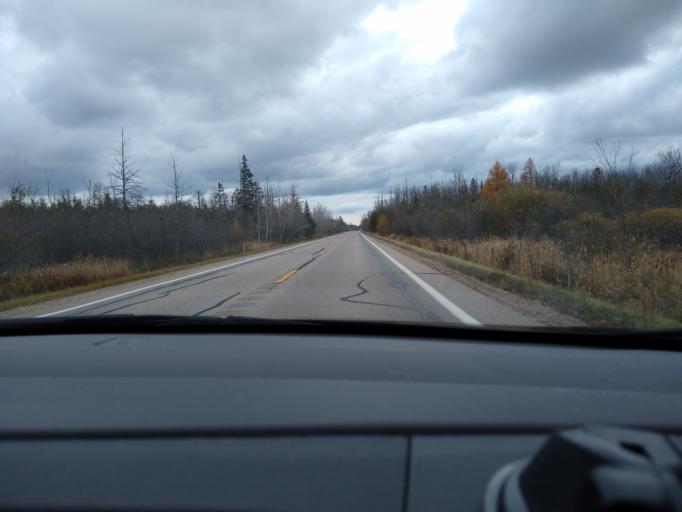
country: US
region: Michigan
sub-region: Delta County
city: Escanaba
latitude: 45.7327
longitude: -87.2639
